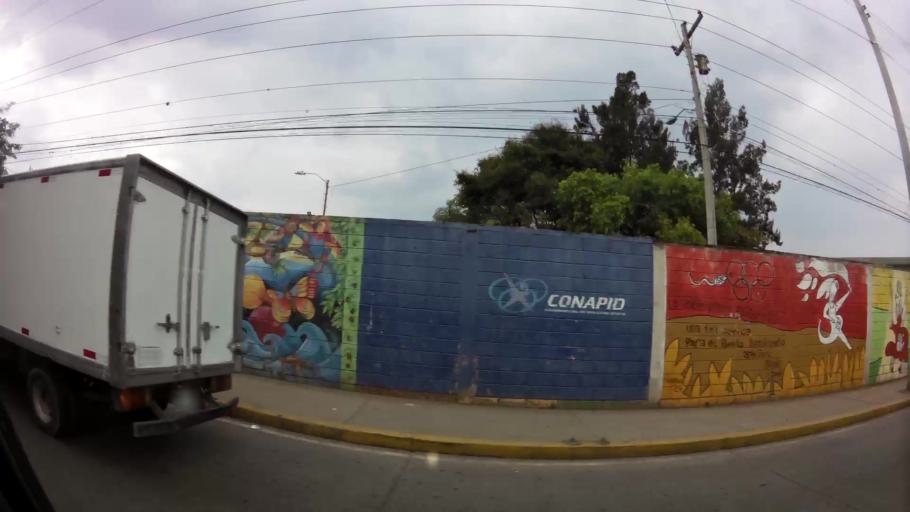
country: HN
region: Francisco Morazan
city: Santa Lucia
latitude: 14.0911
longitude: -87.1613
